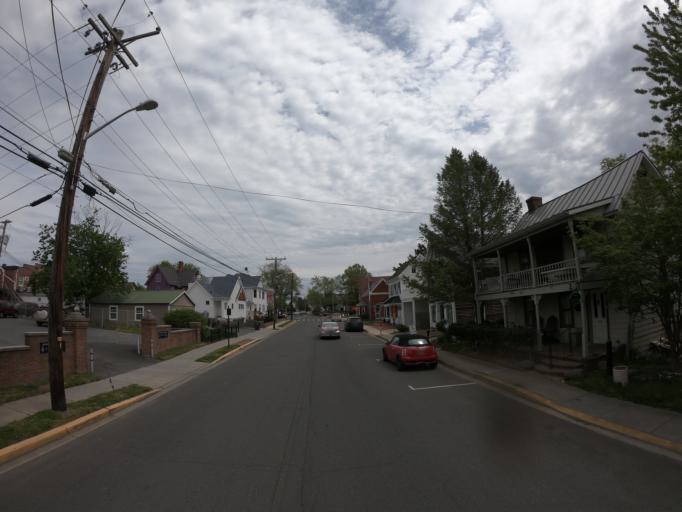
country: US
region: Delaware
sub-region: Sussex County
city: Lewes
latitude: 38.7746
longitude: -75.1400
